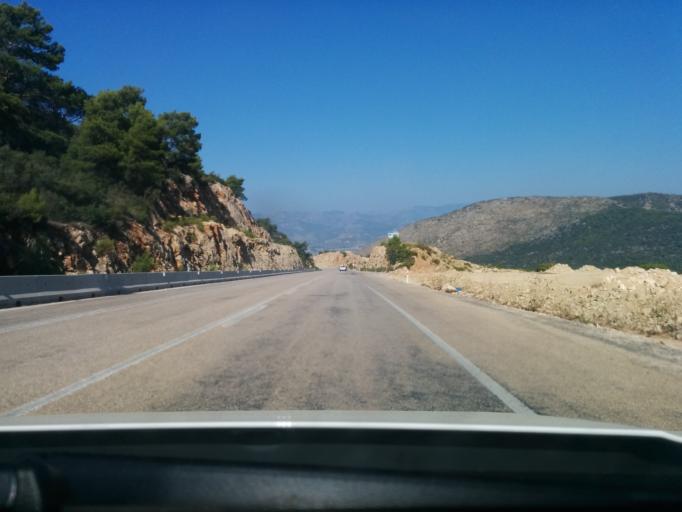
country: TR
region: Antalya
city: Kalkan
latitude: 36.2762
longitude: 29.3924
